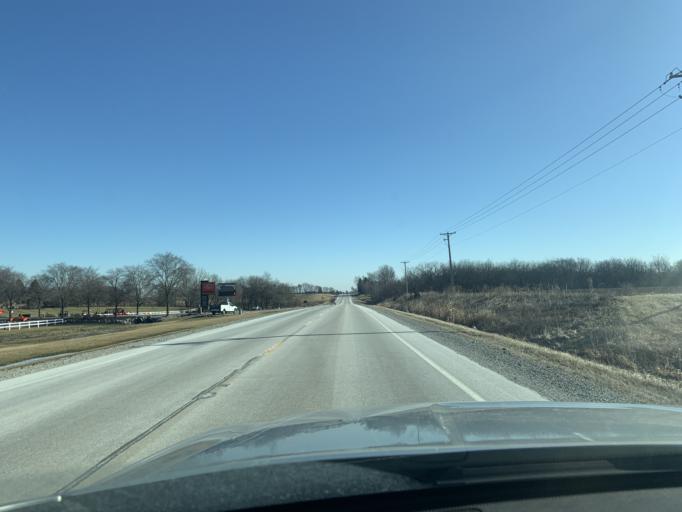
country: US
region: Illinois
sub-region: Grundy County
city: Morris
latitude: 41.3705
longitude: -88.5131
